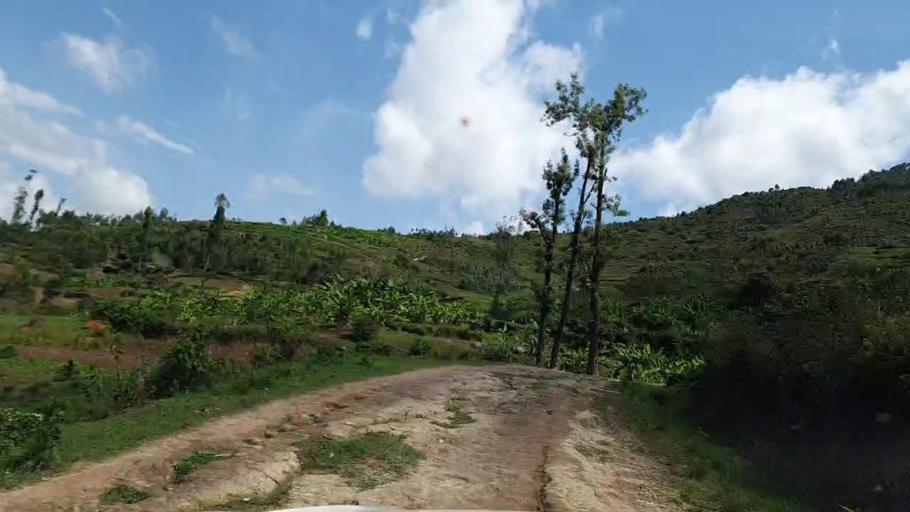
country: RW
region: Southern Province
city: Gikongoro
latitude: -2.3621
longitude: 29.5316
